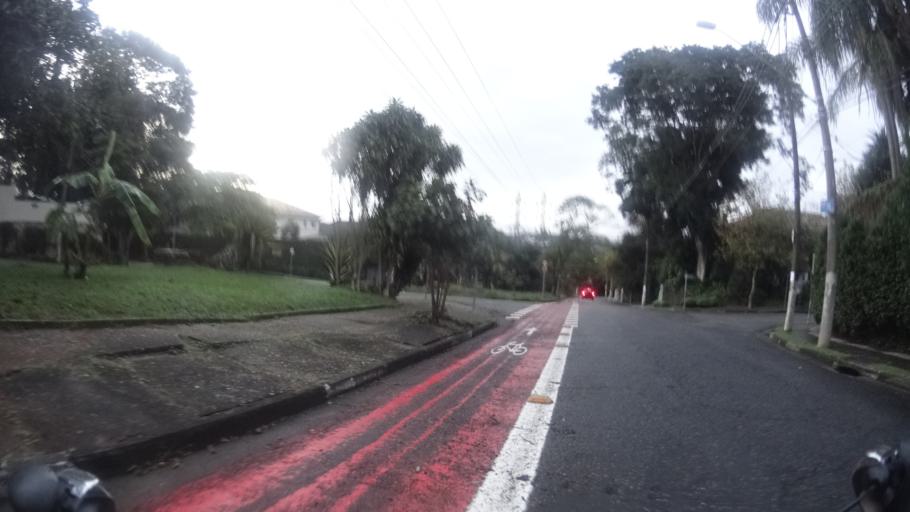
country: BR
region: Sao Paulo
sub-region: Sao Paulo
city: Sao Paulo
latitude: -23.5807
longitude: -46.7083
